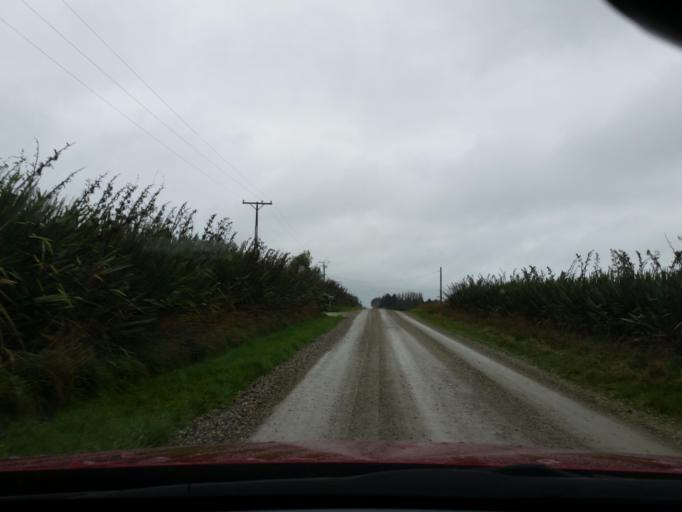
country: NZ
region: Southland
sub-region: Invercargill City
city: Invercargill
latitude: -46.2850
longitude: 168.5067
